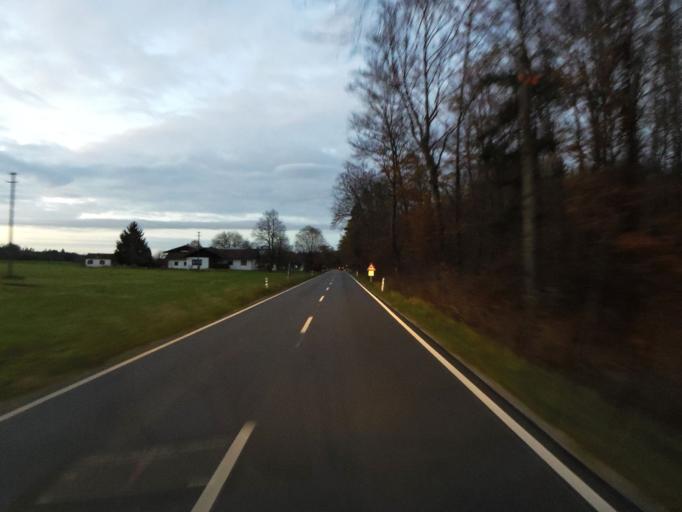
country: DE
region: Bavaria
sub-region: Upper Bavaria
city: Valley
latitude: 47.9307
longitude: 11.7571
